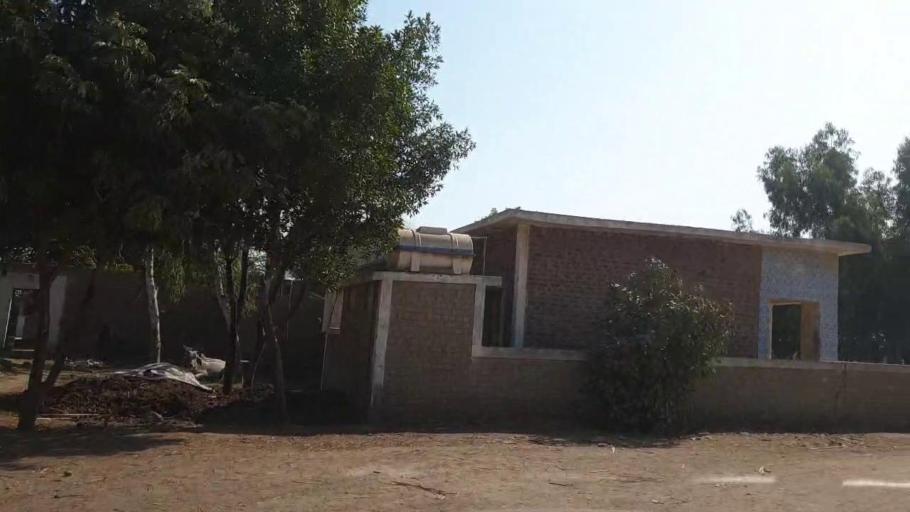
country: PK
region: Sindh
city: Tando Allahyar
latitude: 25.4865
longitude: 68.6994
